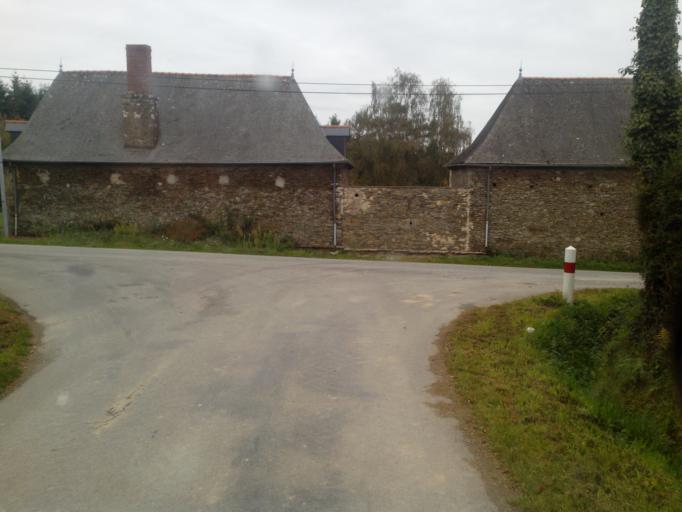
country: FR
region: Brittany
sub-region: Departement du Morbihan
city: Mauron
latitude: 48.0641
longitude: -2.3106
